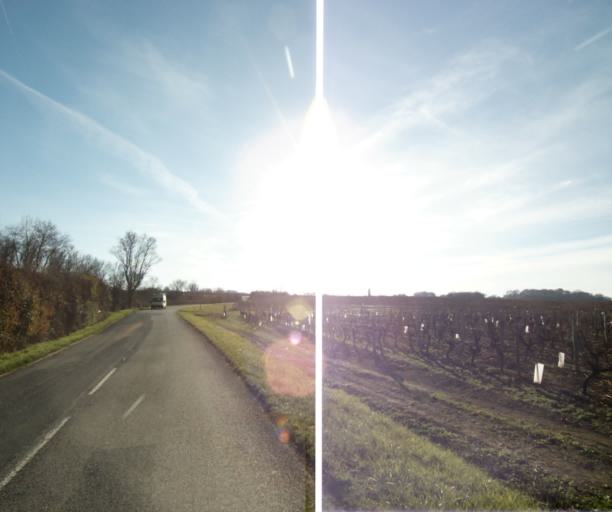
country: FR
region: Poitou-Charentes
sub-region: Departement de la Charente-Maritime
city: Burie
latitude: 45.7833
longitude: -0.4033
